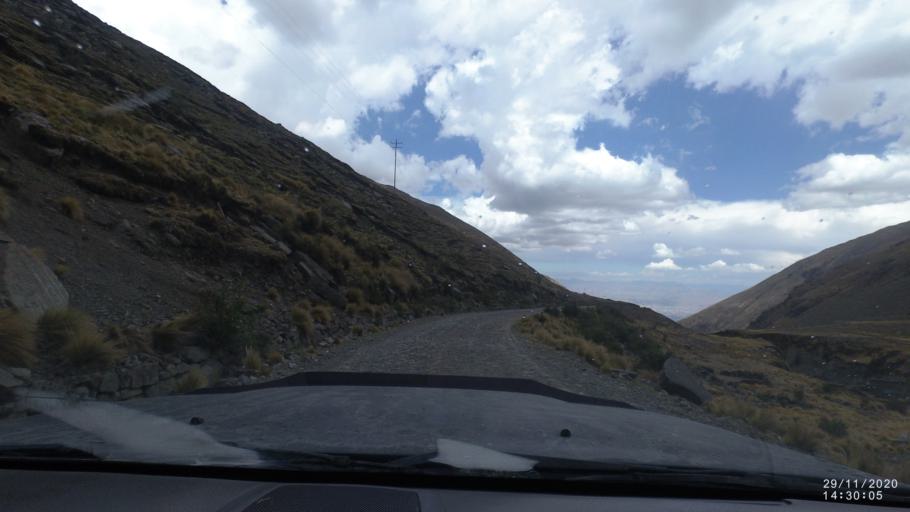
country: BO
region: Cochabamba
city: Sipe Sipe
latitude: -17.2629
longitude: -66.3513
